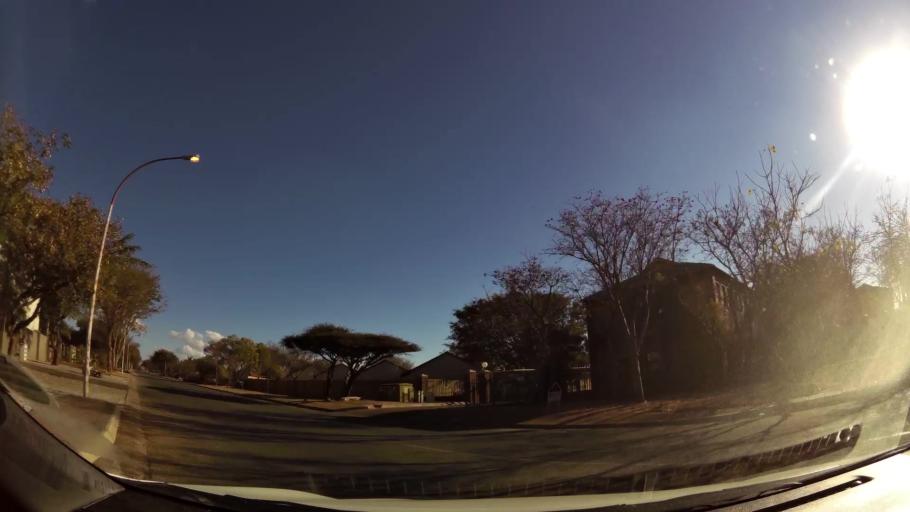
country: ZA
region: Limpopo
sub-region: Capricorn District Municipality
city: Polokwane
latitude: -23.8864
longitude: 29.4877
